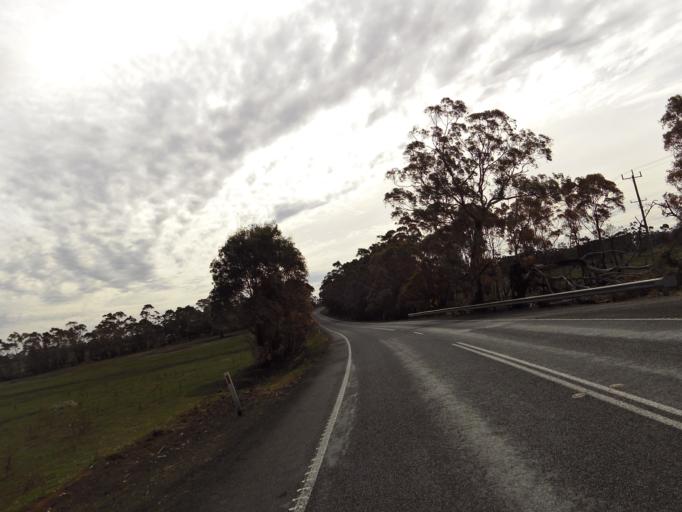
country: AU
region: Victoria
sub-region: Warrnambool
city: Allansford
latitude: -38.3835
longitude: 143.0118
